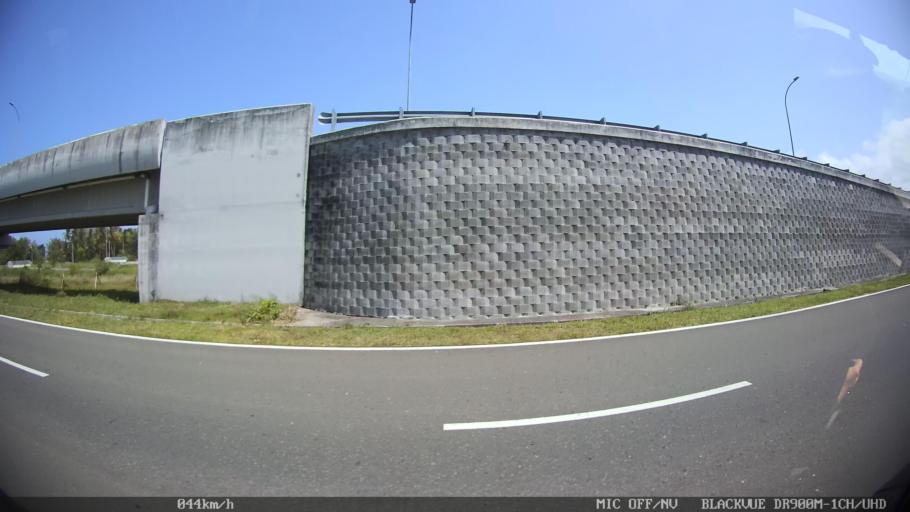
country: ID
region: Daerah Istimewa Yogyakarta
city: Srandakan
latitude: -7.8948
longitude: 110.0572
